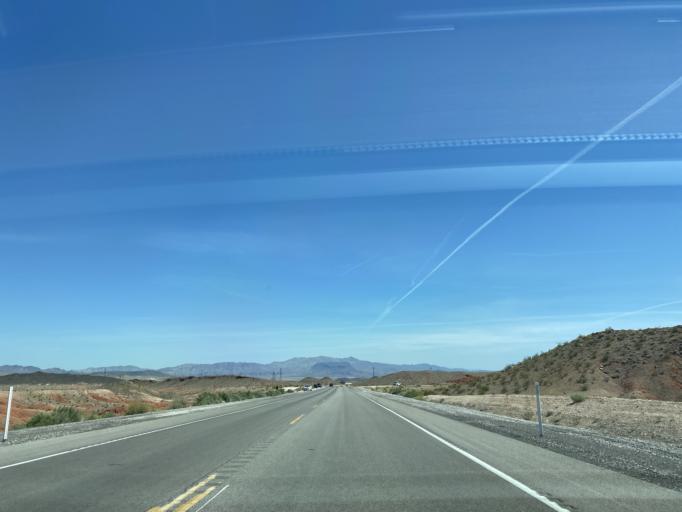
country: US
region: Nevada
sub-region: Clark County
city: Nellis Air Force Base
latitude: 36.1981
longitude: -114.9319
